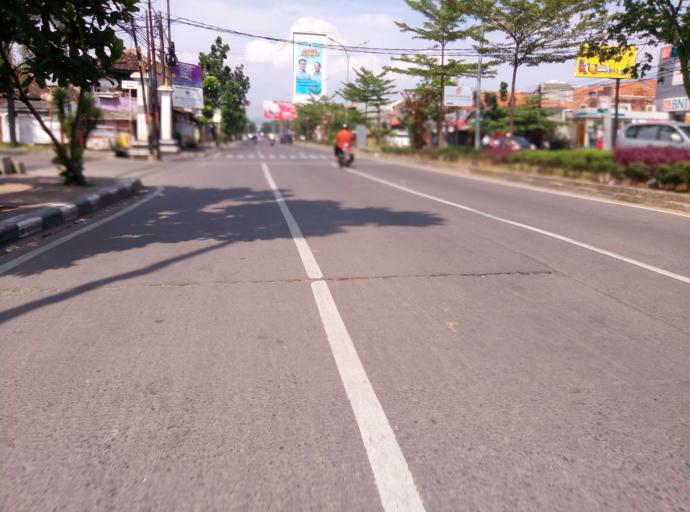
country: ID
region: West Java
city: Bandung
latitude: -6.9428
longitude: 107.6422
